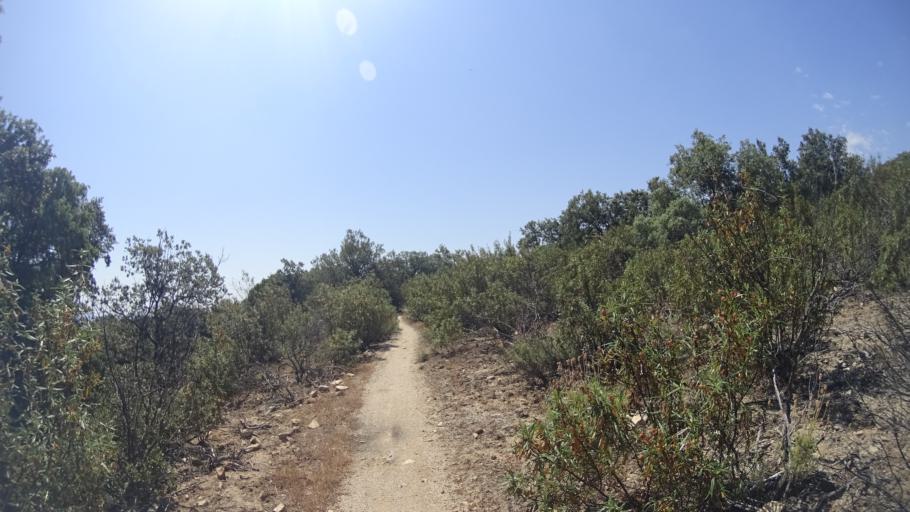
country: ES
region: Madrid
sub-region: Provincia de Madrid
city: Torrelodones
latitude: 40.5980
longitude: -3.9257
